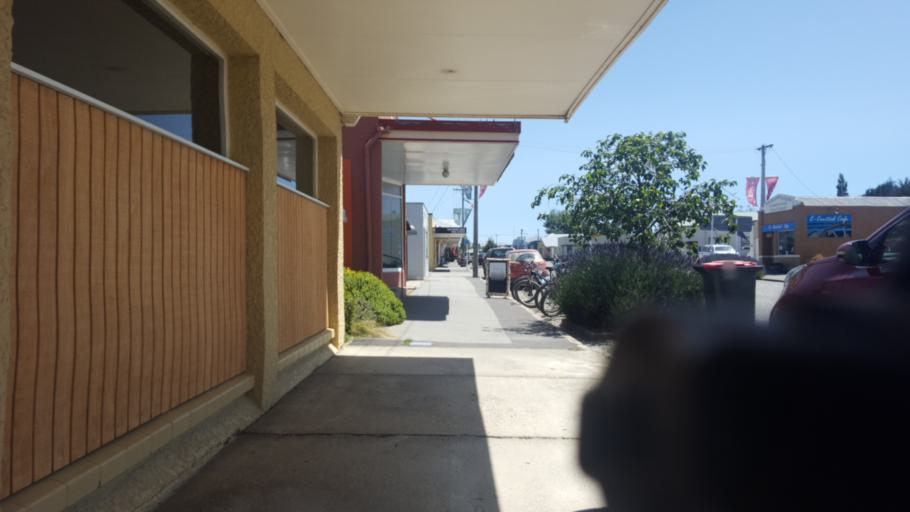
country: NZ
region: Otago
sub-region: Dunedin City
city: Dunedin
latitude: -45.1300
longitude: 170.0992
